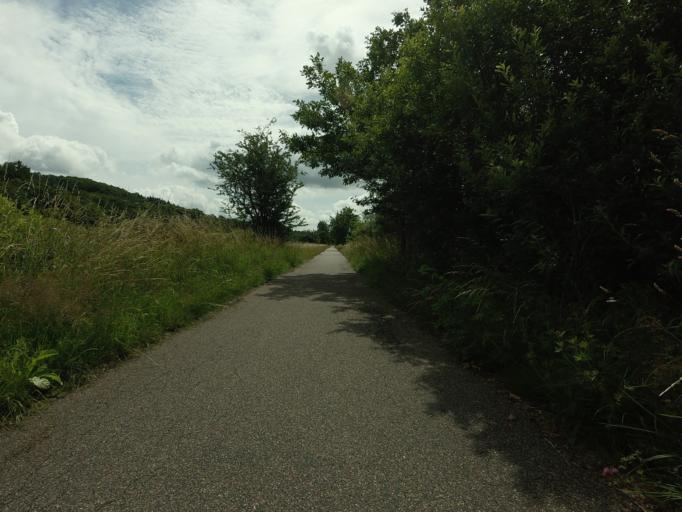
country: DK
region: Central Jutland
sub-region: Randers Kommune
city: Langa
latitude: 56.3734
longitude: 9.8981
